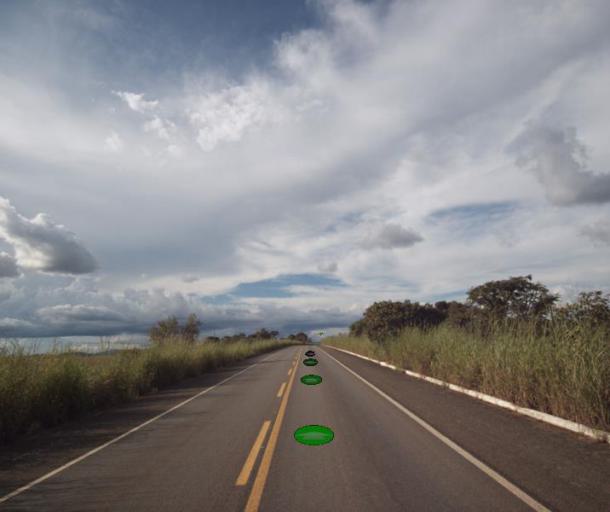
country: BR
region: Goias
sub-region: Niquelandia
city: Niquelandia
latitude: -14.7495
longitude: -48.6201
